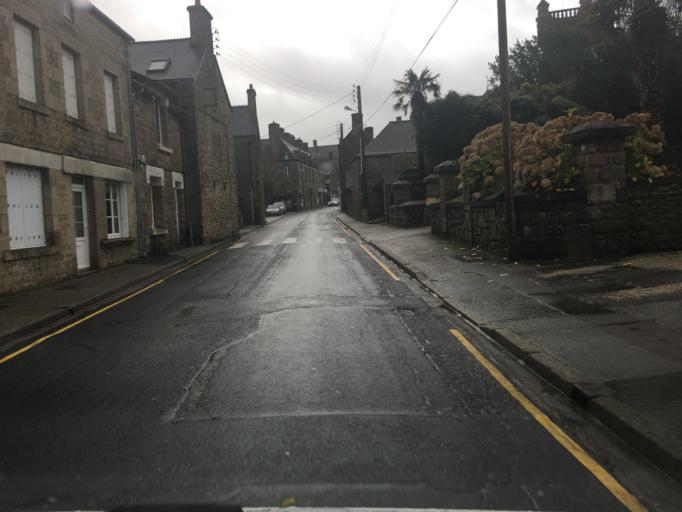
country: FR
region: Lower Normandy
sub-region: Departement de la Manche
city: Saint-Pierre-Eglise
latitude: 49.6699
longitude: -1.4052
